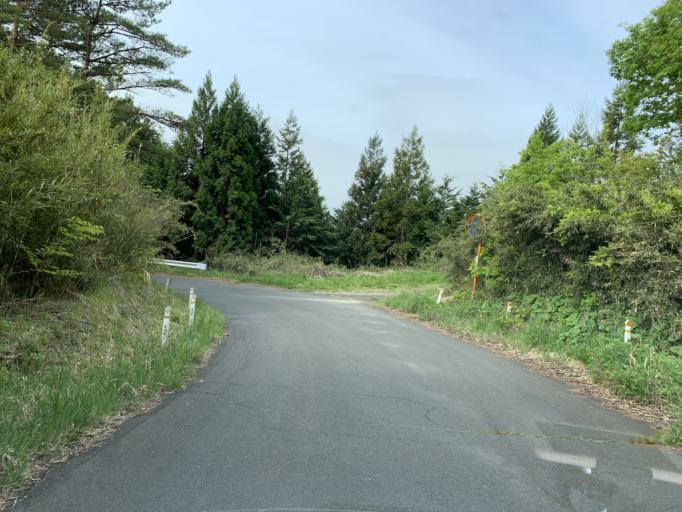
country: JP
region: Iwate
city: Ichinoseki
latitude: 38.8716
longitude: 141.0653
